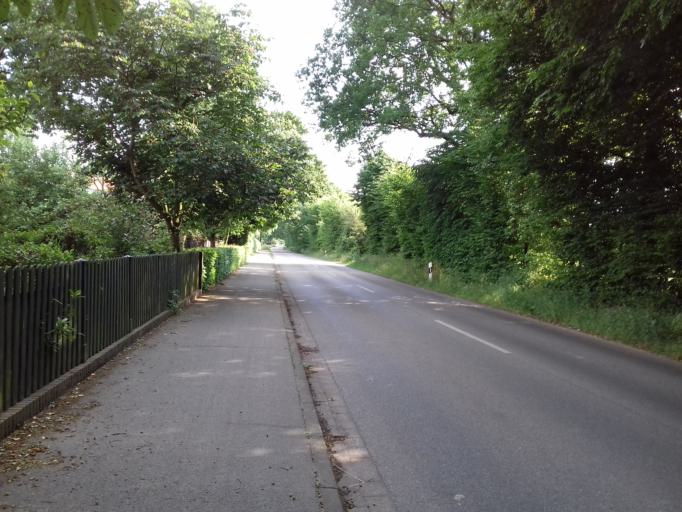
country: DE
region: Schleswig-Holstein
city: Tasdorf
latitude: 54.0833
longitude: 10.0215
